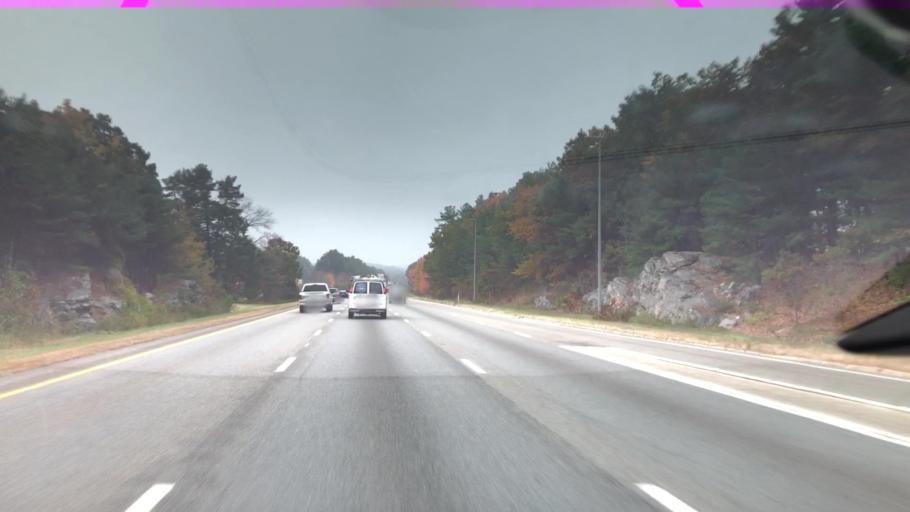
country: US
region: Massachusetts
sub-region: Worcester County
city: Harvard
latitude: 42.4838
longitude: -71.5475
